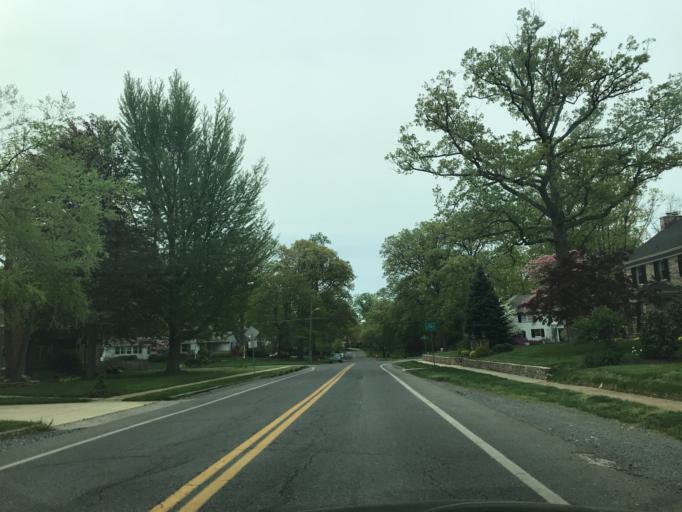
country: US
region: Maryland
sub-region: Baltimore County
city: Catonsville
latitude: 39.2617
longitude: -76.7463
